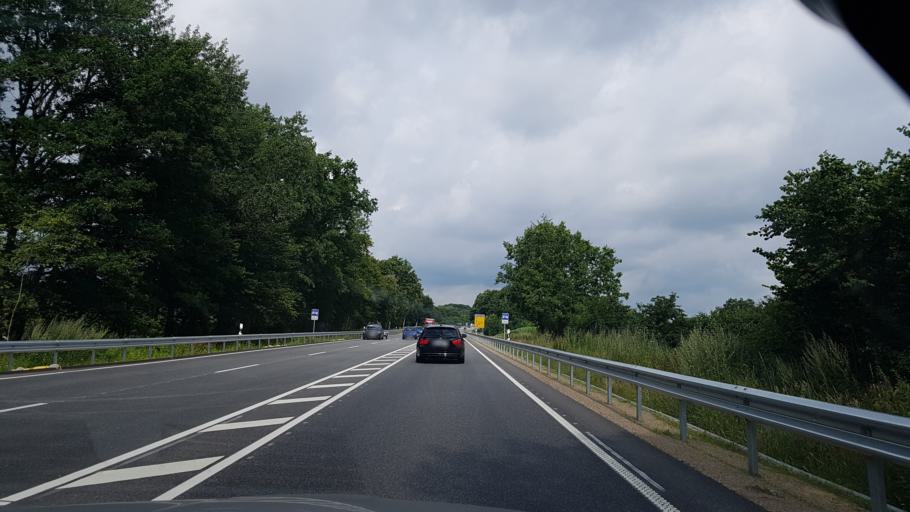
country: DE
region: Schleswig-Holstein
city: Gronwohld
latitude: 53.6606
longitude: 10.3907
